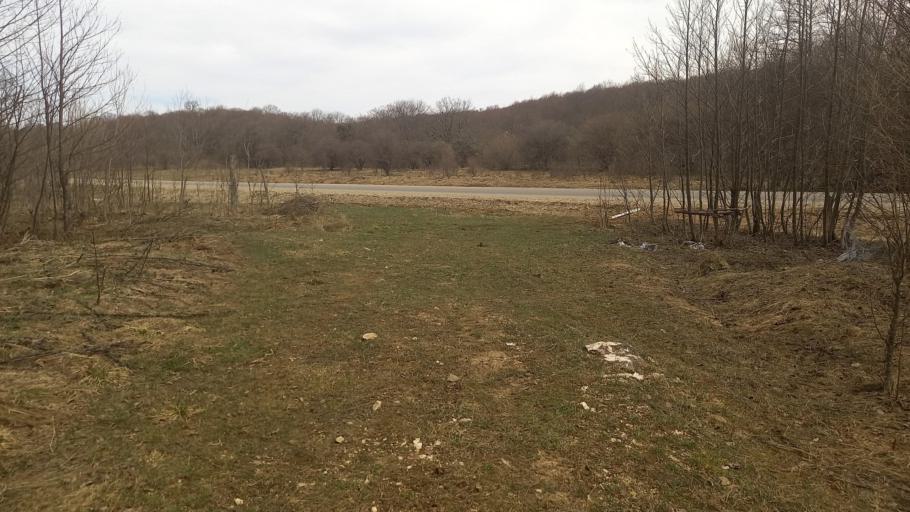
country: RU
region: Adygeya
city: Kamennomostskiy
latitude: 44.2191
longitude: 40.0843
